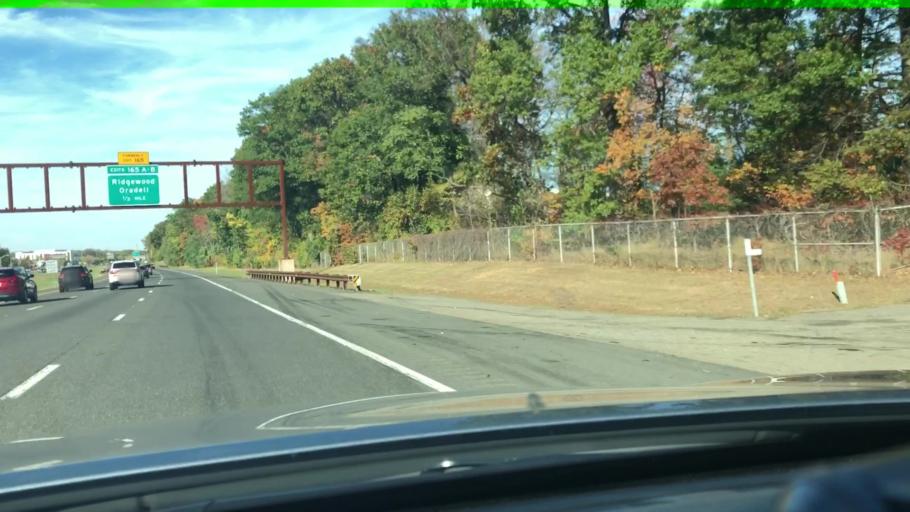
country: US
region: New Jersey
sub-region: Bergen County
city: Paramus
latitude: 40.9518
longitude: -74.0657
